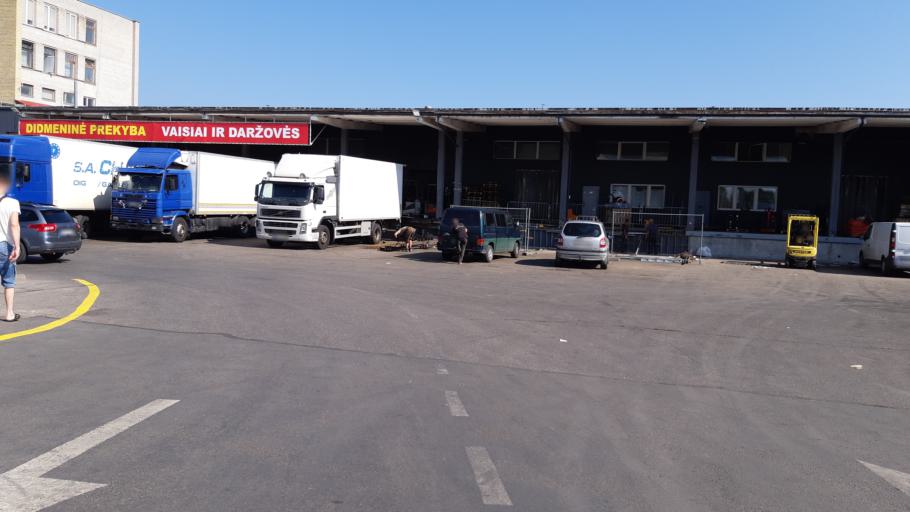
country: LT
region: Kauno apskritis
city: Dainava (Kaunas)
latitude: 54.9146
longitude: 23.9955
